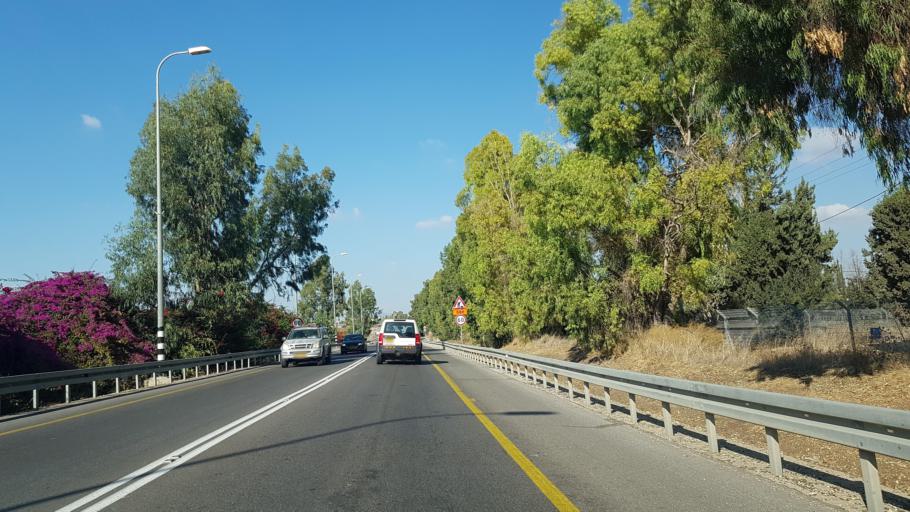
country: PS
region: West Bank
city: Tulkarm
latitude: 32.3296
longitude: 35.0032
